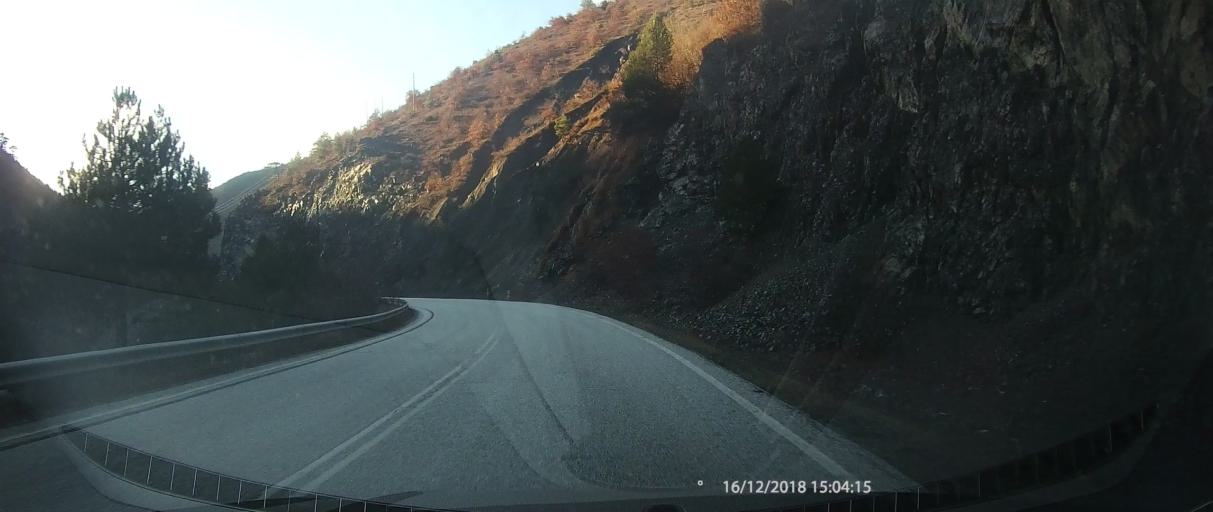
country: GR
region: West Macedonia
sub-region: Nomos Kastorias
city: Nestorio
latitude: 40.2282
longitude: 20.9716
